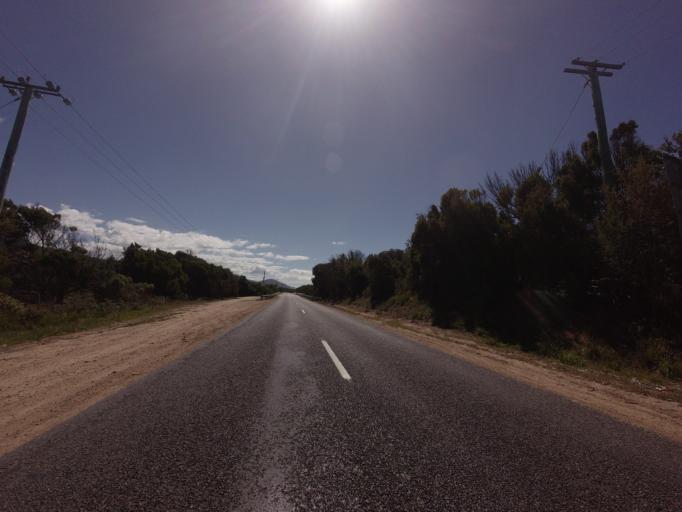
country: AU
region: Tasmania
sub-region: Break O'Day
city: St Helens
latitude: -41.8149
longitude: 148.2629
